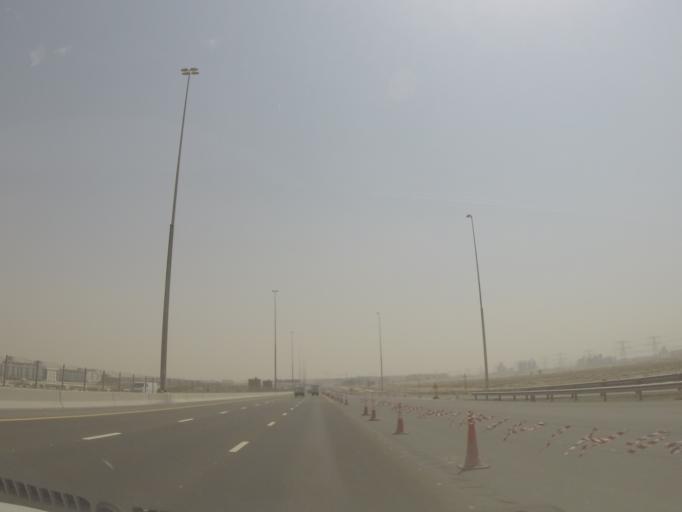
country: AE
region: Dubai
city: Dubai
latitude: 25.0114
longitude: 55.1546
